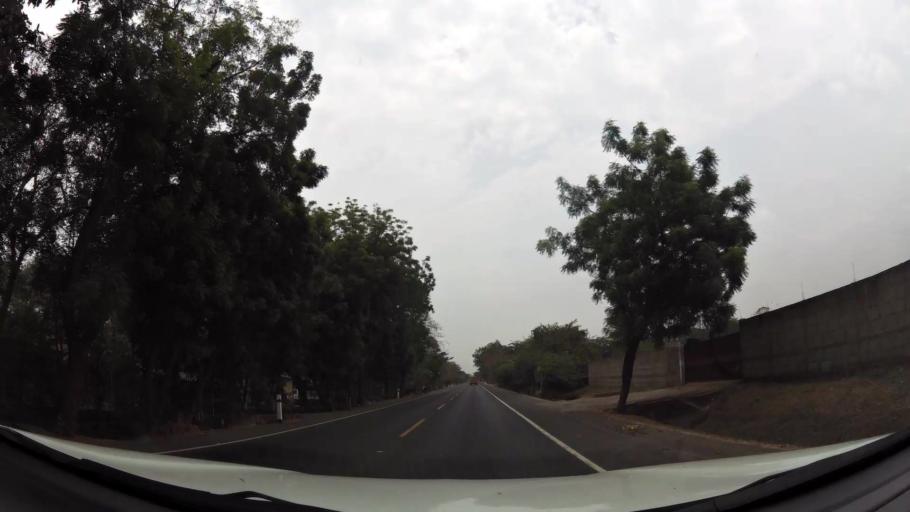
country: NI
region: Chinandega
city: Chichigalpa
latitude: 12.5951
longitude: -87.0313
